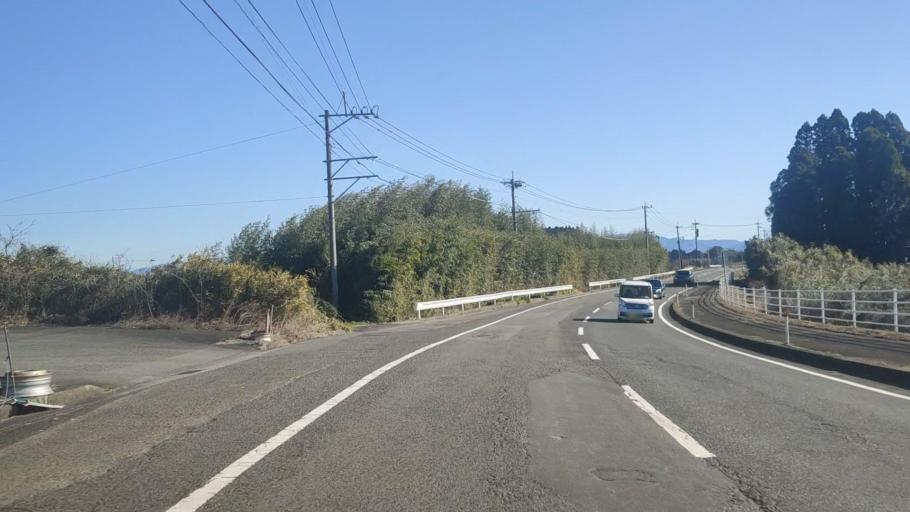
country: JP
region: Kagoshima
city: Sueyoshicho-ninokata
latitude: 31.6881
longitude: 130.9618
